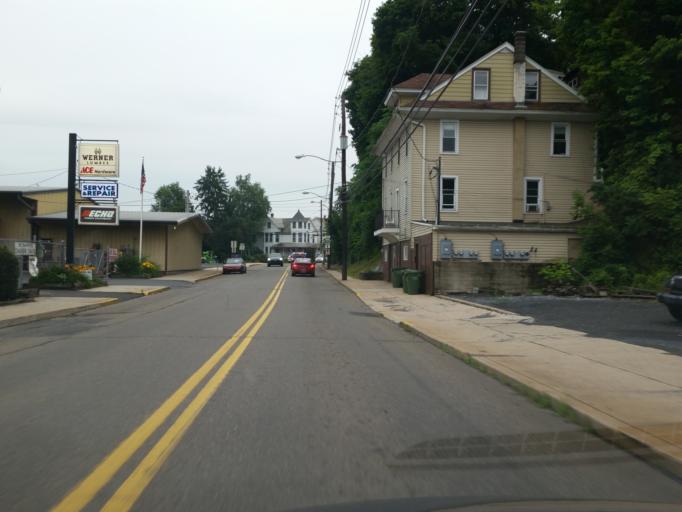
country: US
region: Pennsylvania
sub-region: Schuylkill County
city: Pine Grove
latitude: 40.5532
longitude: -76.3870
